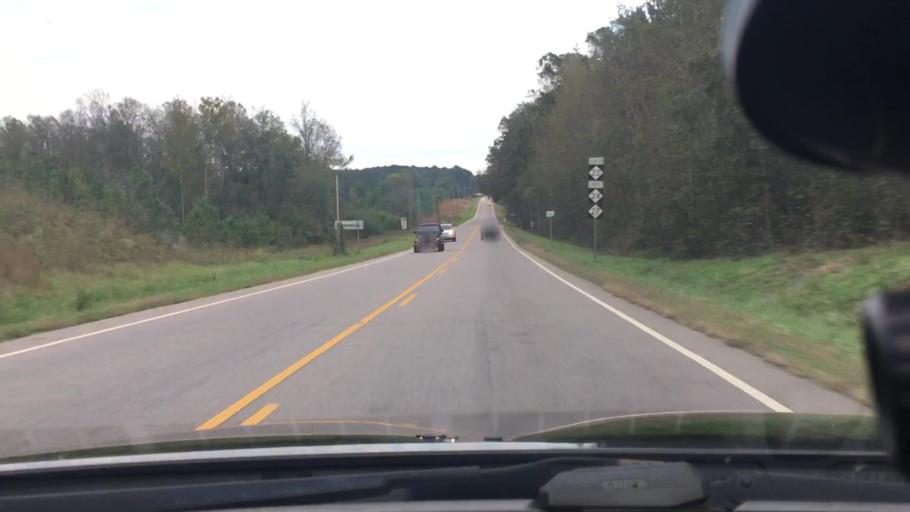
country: US
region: North Carolina
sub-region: Moore County
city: Carthage
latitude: 35.3835
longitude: -79.4869
